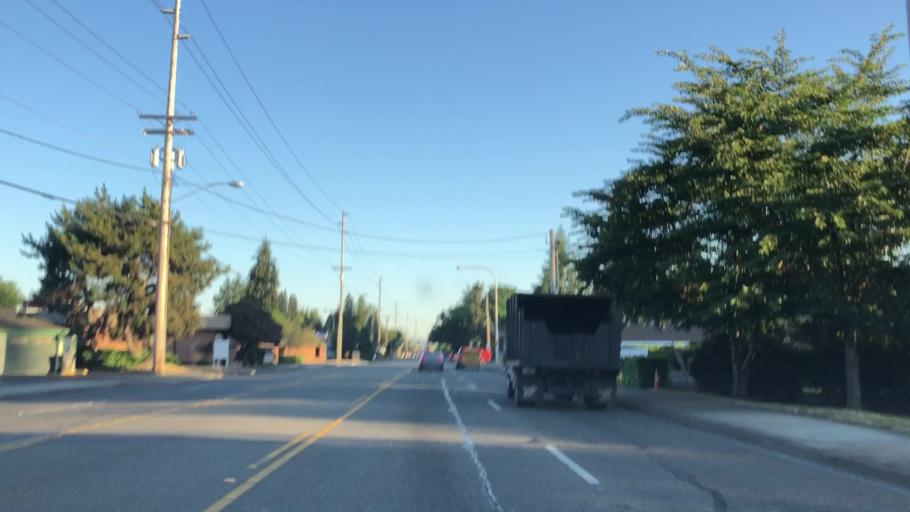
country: US
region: Washington
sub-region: King County
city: Auburn
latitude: 47.3176
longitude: -122.2169
